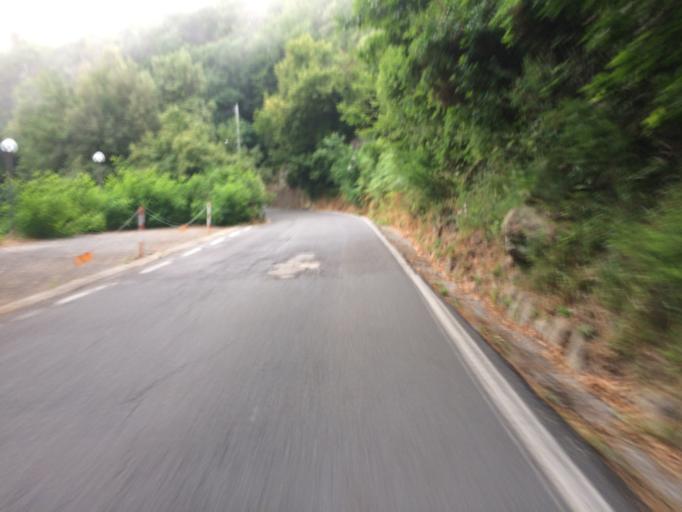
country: IT
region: Liguria
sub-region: Provincia di Imperia
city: Seborga
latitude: 43.8540
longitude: 7.7285
